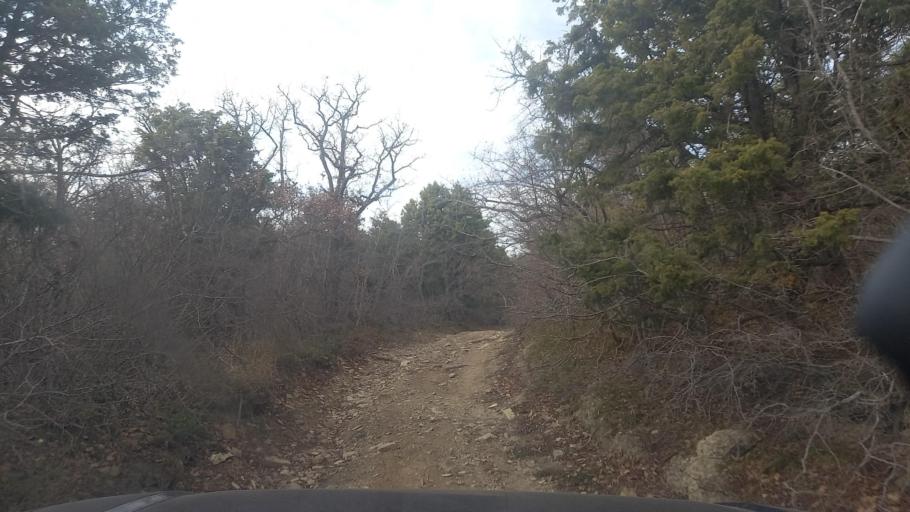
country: RU
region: Krasnodarskiy
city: Myskhako
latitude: 44.6669
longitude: 37.6744
